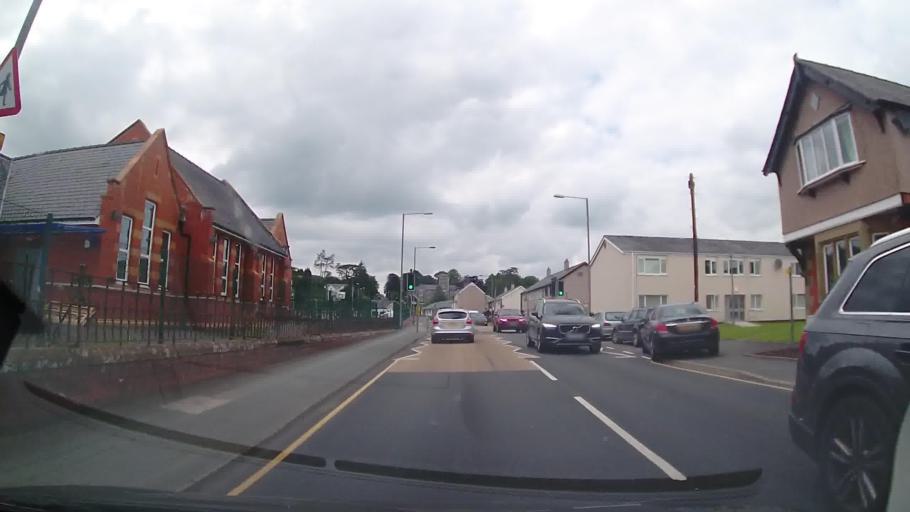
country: GB
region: Wales
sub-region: Gwynedd
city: Bala
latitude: 52.9126
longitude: -3.5970
